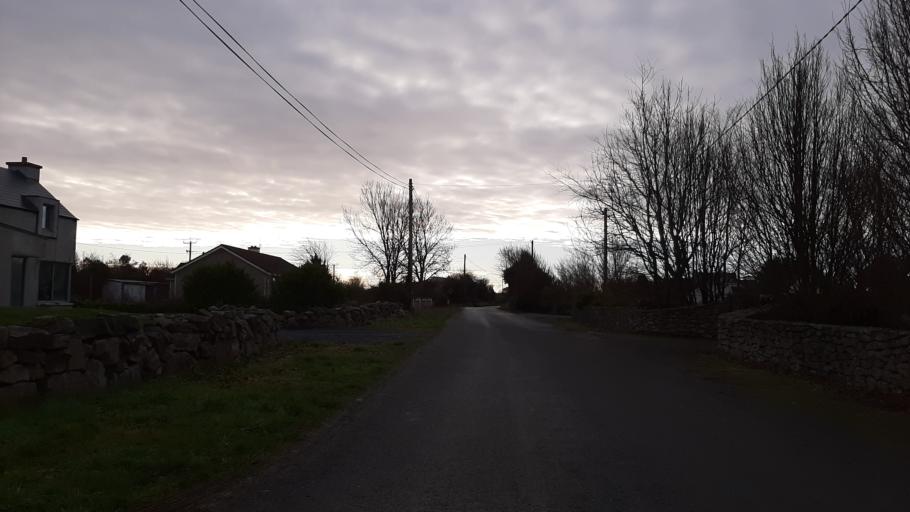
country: IE
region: Connaught
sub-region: County Galway
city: Gaillimh
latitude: 53.3091
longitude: -9.0681
